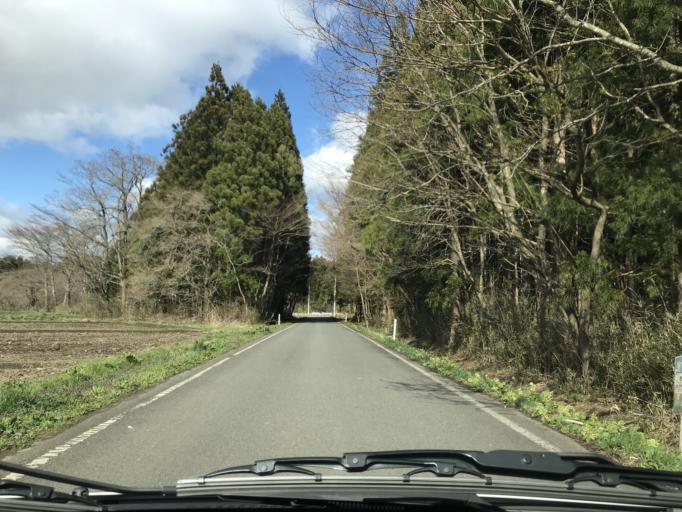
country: JP
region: Iwate
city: Mizusawa
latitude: 39.1039
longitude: 141.0911
